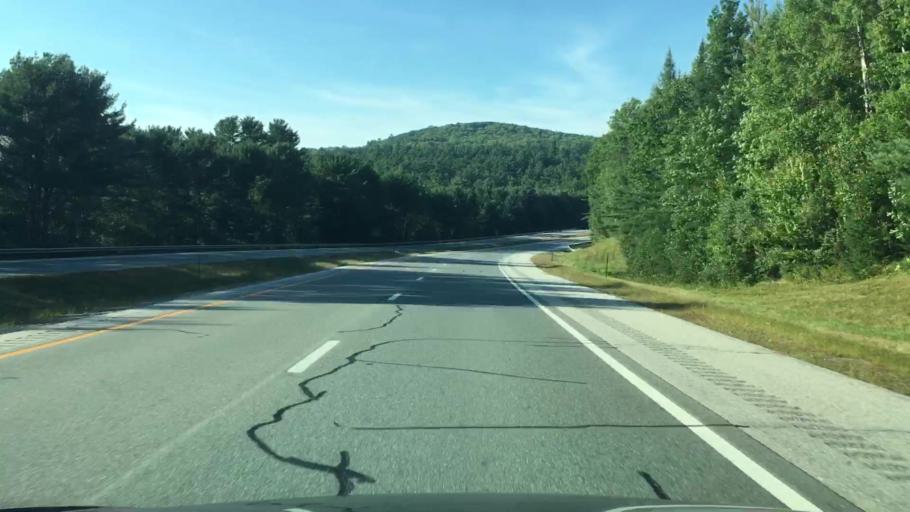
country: US
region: New Hampshire
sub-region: Grafton County
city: Littleton
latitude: 44.2450
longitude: -71.7601
